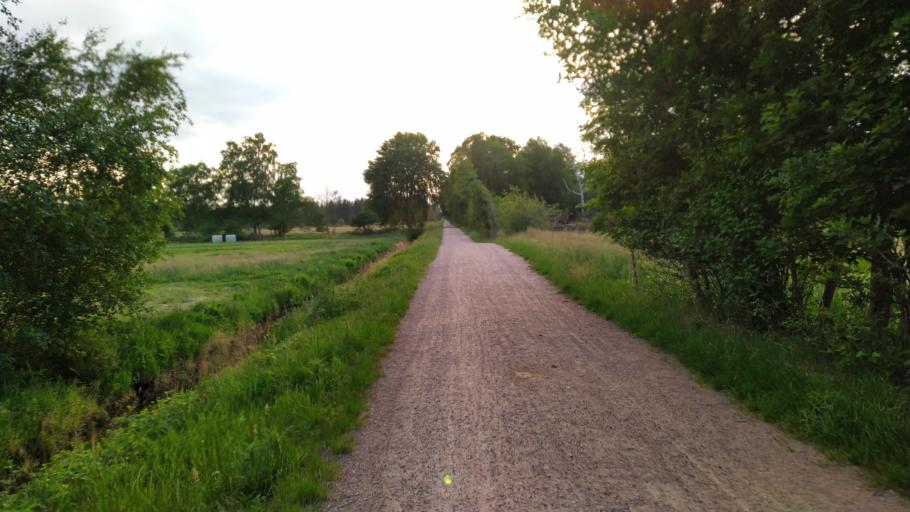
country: DE
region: Lower Saxony
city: Buxtehude
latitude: 53.4796
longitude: 9.6671
